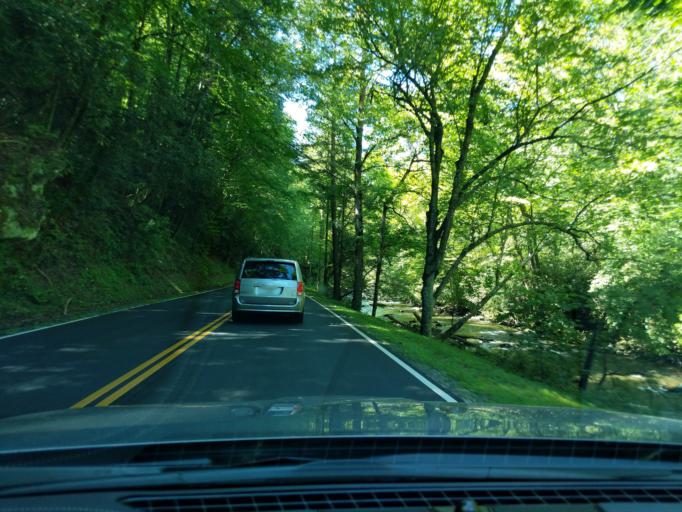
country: US
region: North Carolina
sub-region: Swain County
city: Cherokee
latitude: 35.5456
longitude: -83.3052
